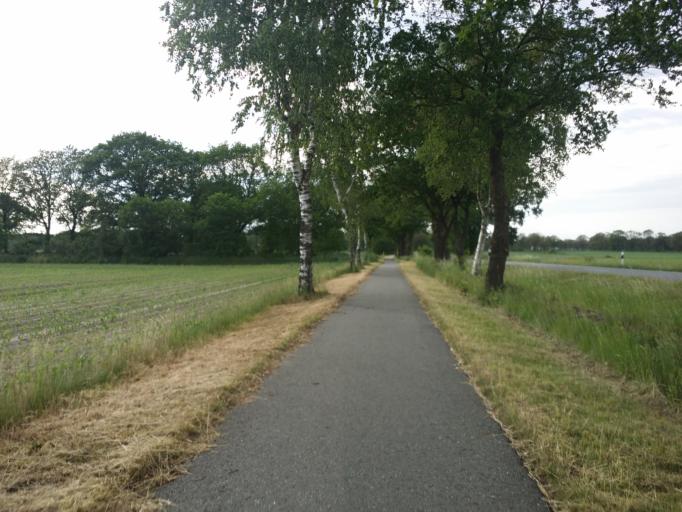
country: DE
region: Lower Saxony
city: Friedeburg
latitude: 53.4189
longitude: 7.8771
